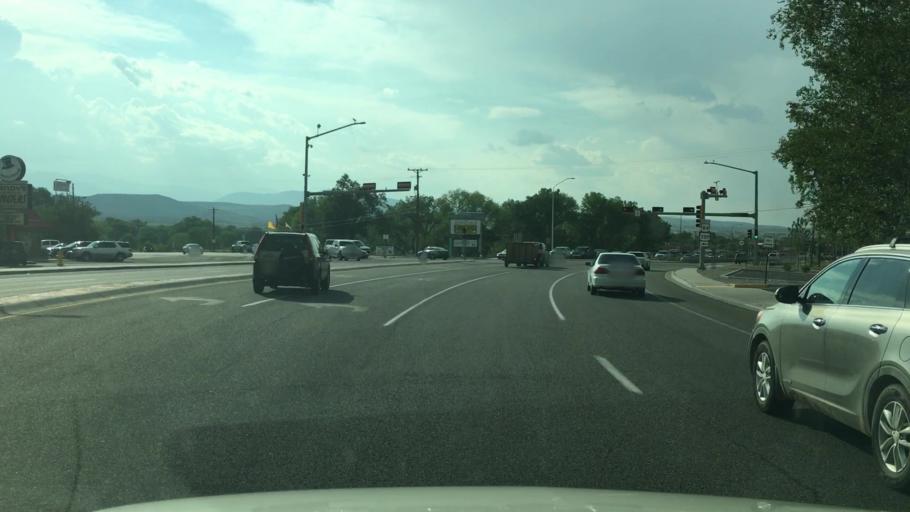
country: US
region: New Mexico
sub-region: Rio Arriba County
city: Espanola
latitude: 35.9884
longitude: -106.0648
